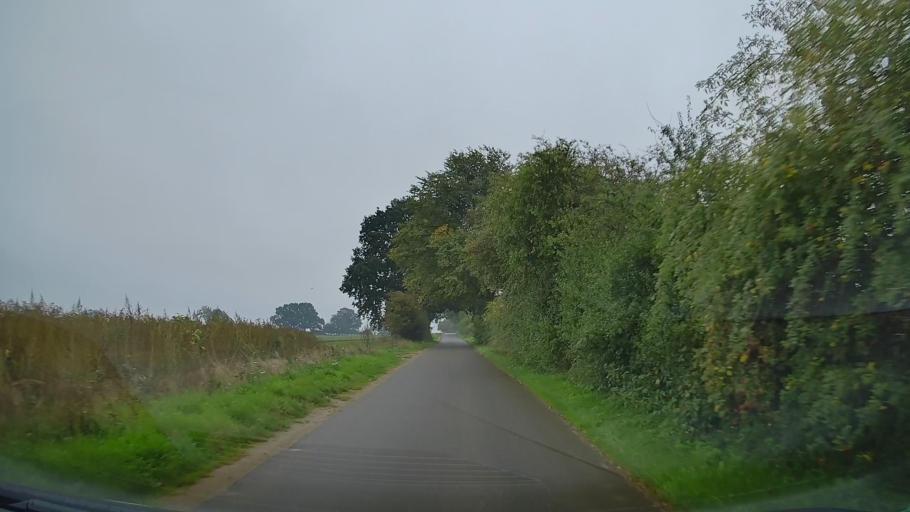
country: DE
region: Mecklenburg-Vorpommern
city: Gramkow
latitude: 53.9259
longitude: 11.3402
